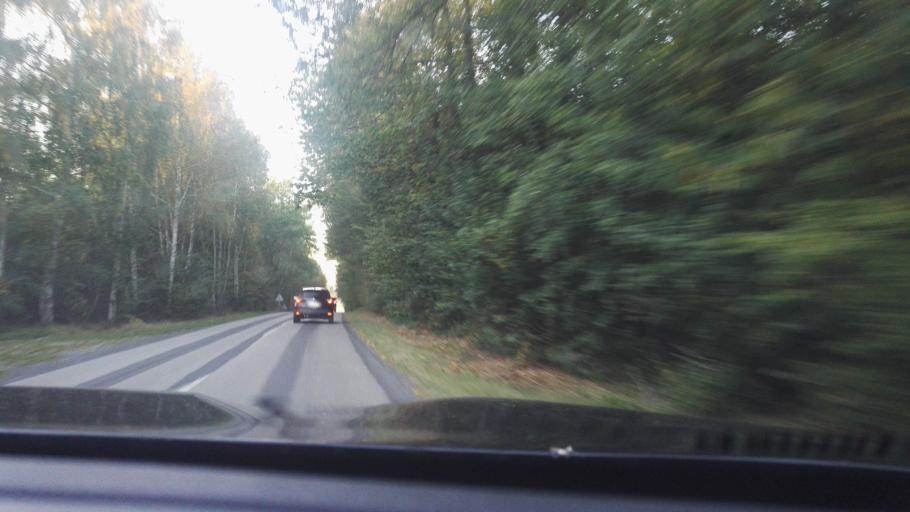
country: FR
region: Ile-de-France
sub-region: Departement des Yvelines
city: Houdan
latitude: 48.8504
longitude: 1.5951
